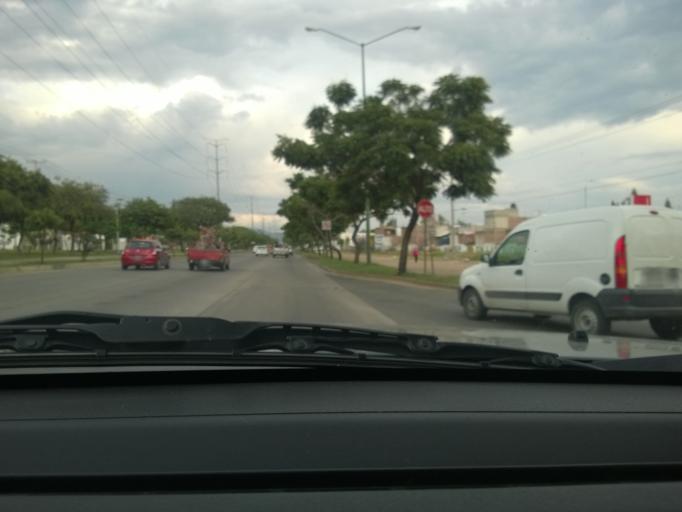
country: MX
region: Guanajuato
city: Leon
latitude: 21.1492
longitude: -101.6628
